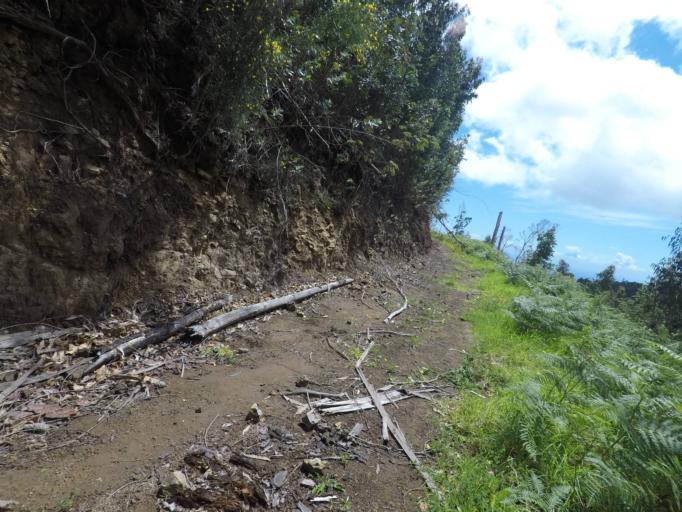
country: PT
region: Madeira
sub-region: Calheta
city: Estreito da Calheta
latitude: 32.7474
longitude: -17.1948
